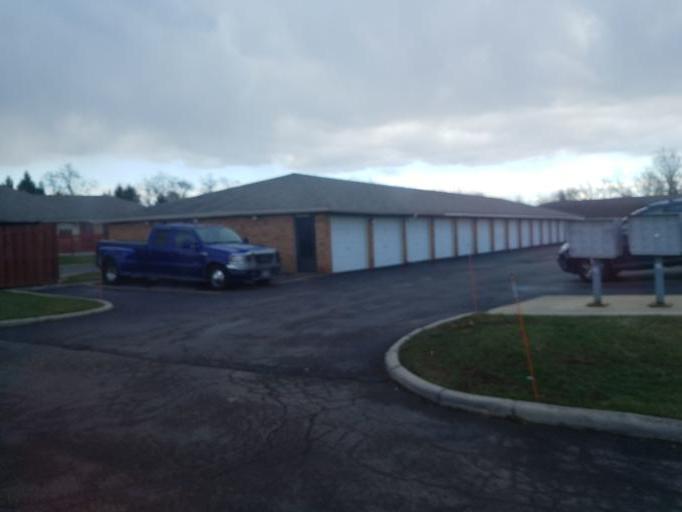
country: US
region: Ohio
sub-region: Delaware County
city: Delaware
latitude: 40.3119
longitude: -83.0982
